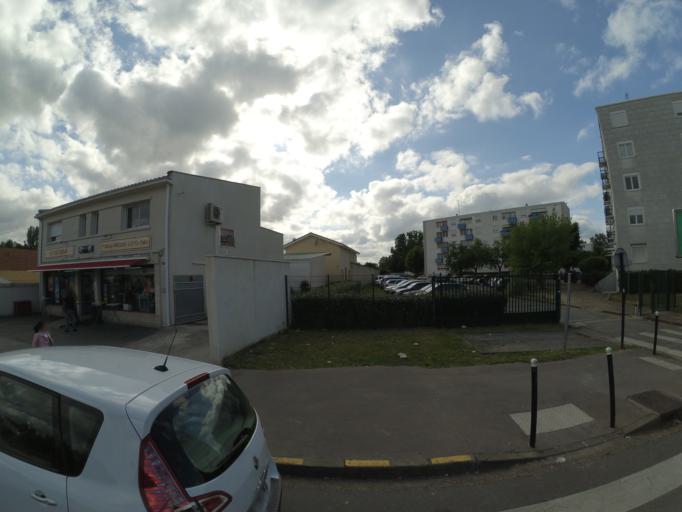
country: FR
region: Aquitaine
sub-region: Departement de la Gironde
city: Lormont
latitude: 44.8799
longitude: -0.5520
